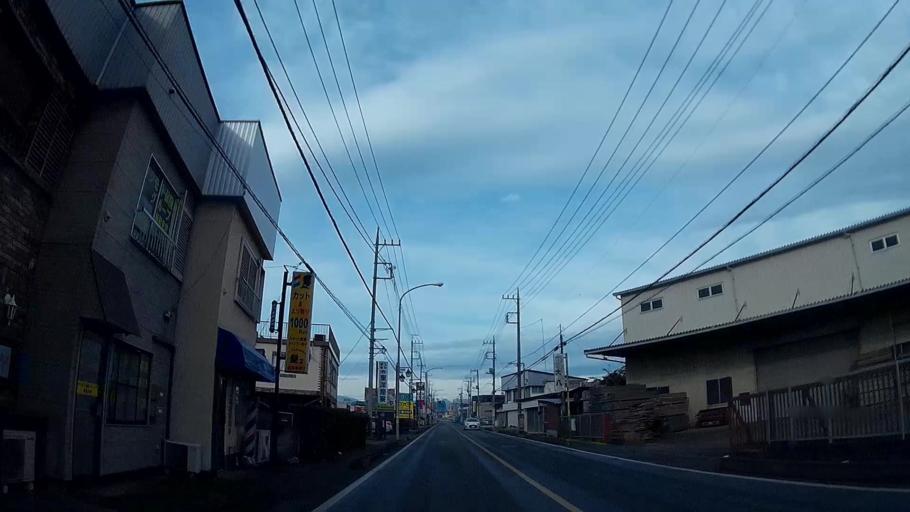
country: JP
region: Saitama
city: Hanno
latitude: 35.8467
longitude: 139.3381
